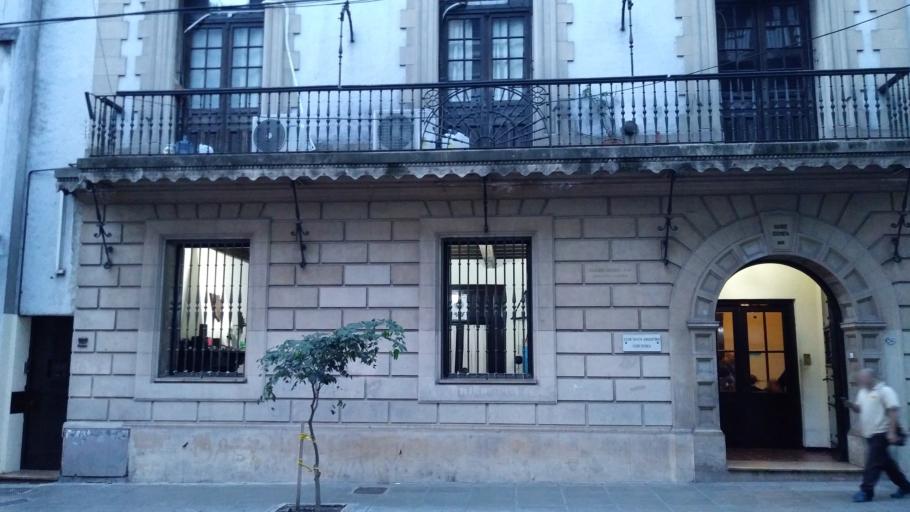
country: AR
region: Buenos Aires F.D.
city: Buenos Aires
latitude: -34.6072
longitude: -58.3971
